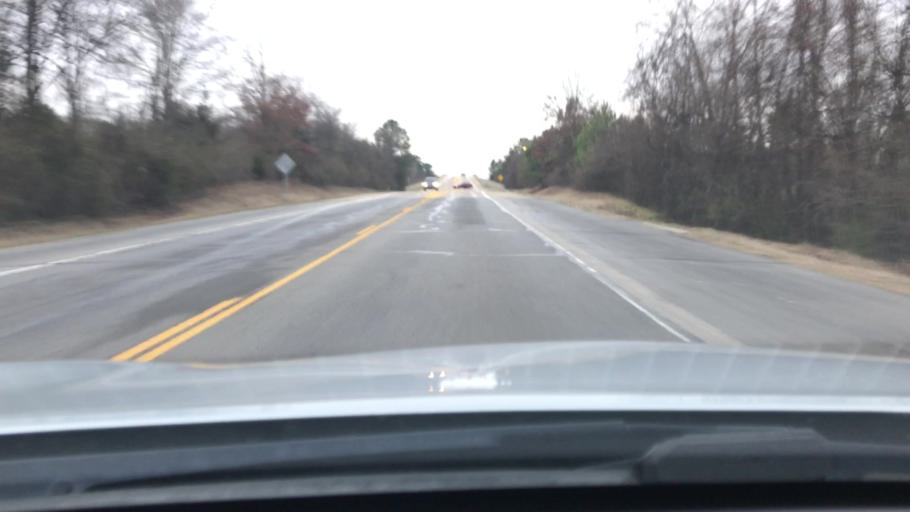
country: US
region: Arkansas
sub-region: Hempstead County
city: Hope
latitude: 33.6781
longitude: -93.5756
